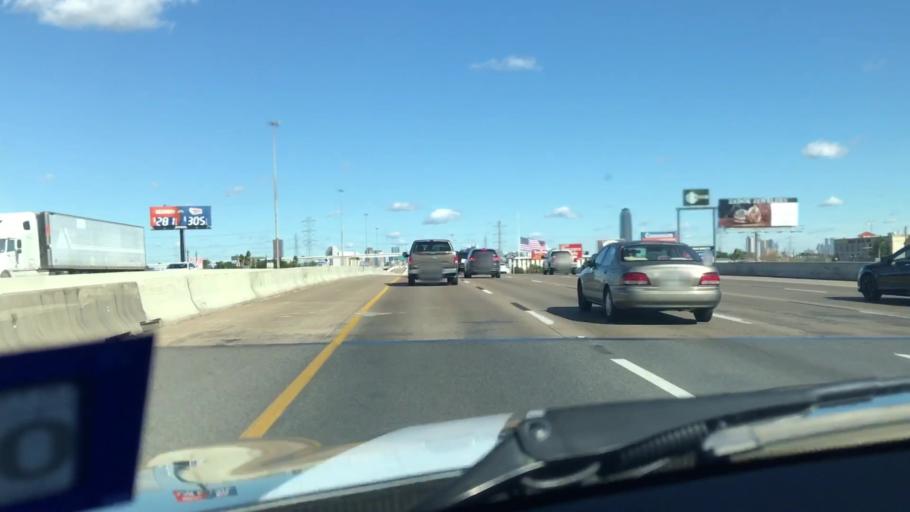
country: US
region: Texas
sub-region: Harris County
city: Bellaire
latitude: 29.7162
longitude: -95.4997
